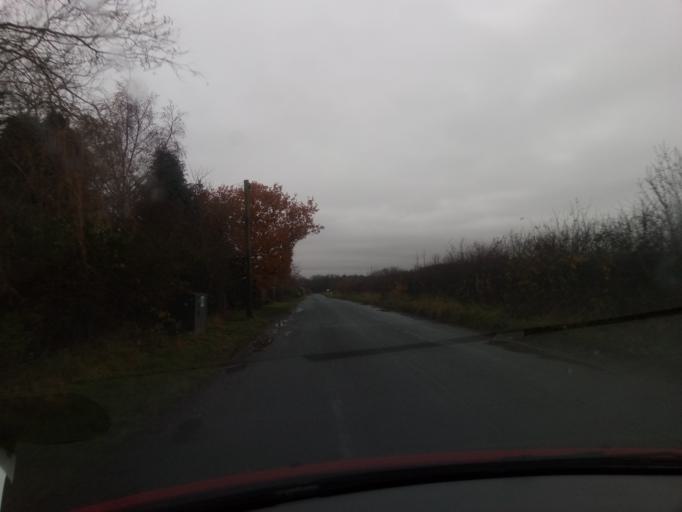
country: GB
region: Scotland
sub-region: The Scottish Borders
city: Saint Boswells
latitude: 55.5596
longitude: -2.6618
